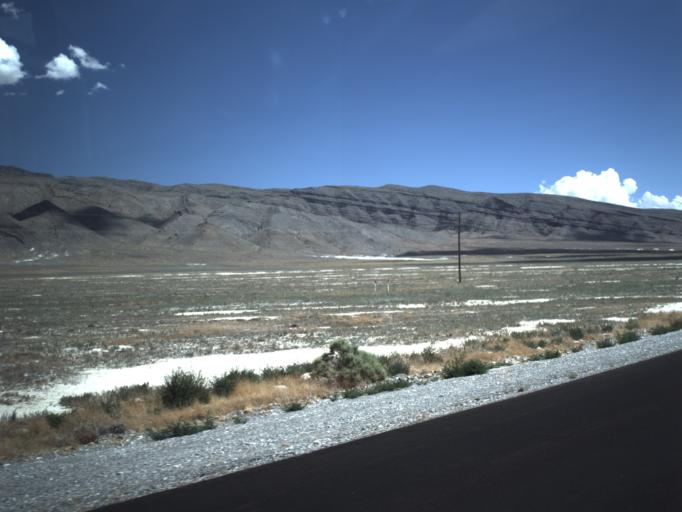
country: US
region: Utah
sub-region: Beaver County
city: Milford
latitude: 39.0672
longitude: -113.4533
